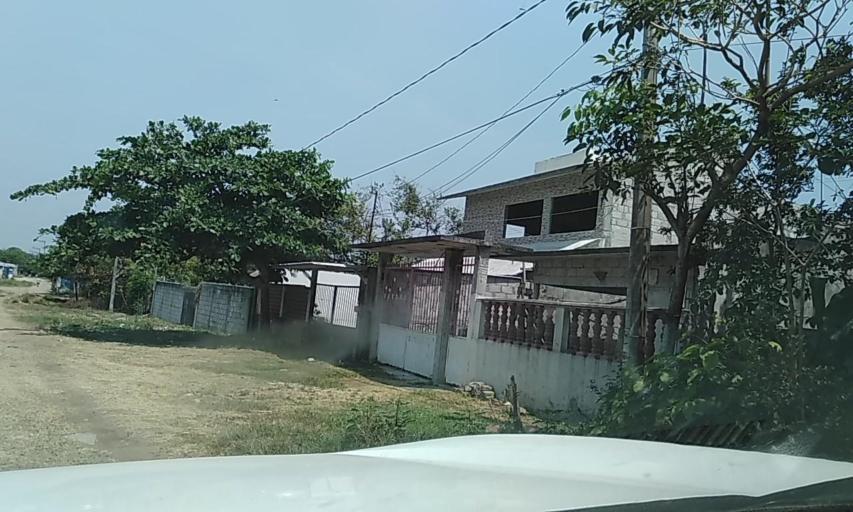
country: MX
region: Veracruz
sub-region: Veracruz
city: Las Amapolas
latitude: 19.1391
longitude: -96.1940
